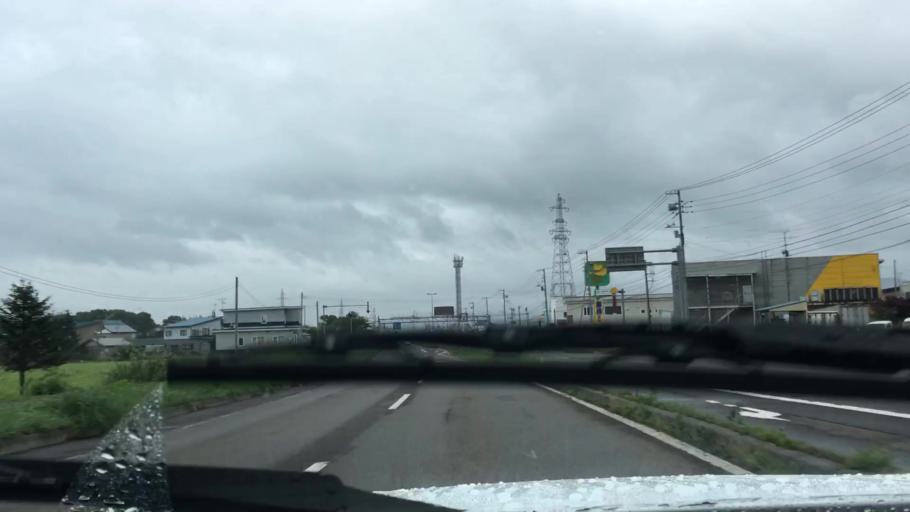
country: JP
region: Hokkaido
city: Nanae
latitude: 42.2612
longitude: 140.2751
